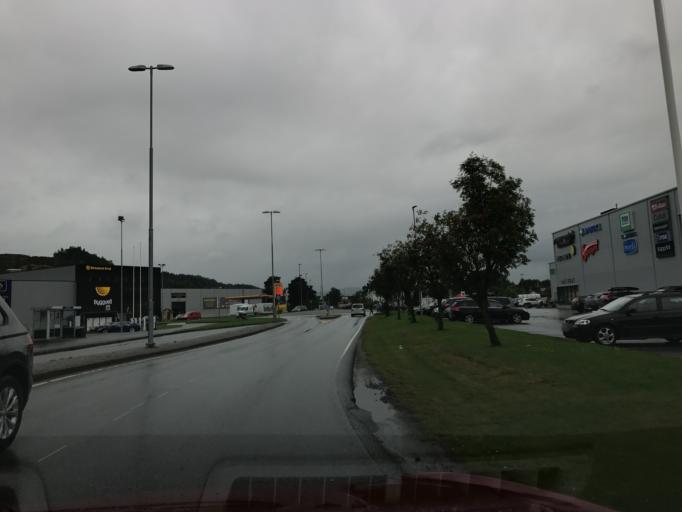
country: NO
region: Vest-Agder
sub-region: Lyngdal
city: Lyngdal
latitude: 58.1562
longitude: 7.1024
